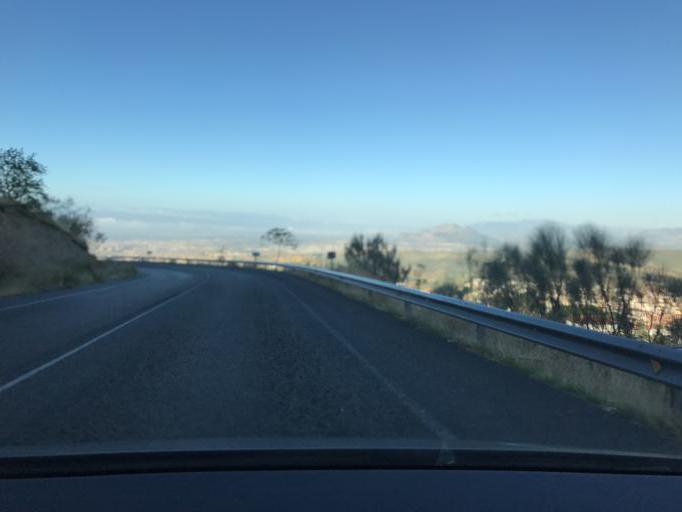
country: ES
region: Andalusia
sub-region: Provincia de Granada
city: Viznar
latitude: 37.2339
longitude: -3.5571
